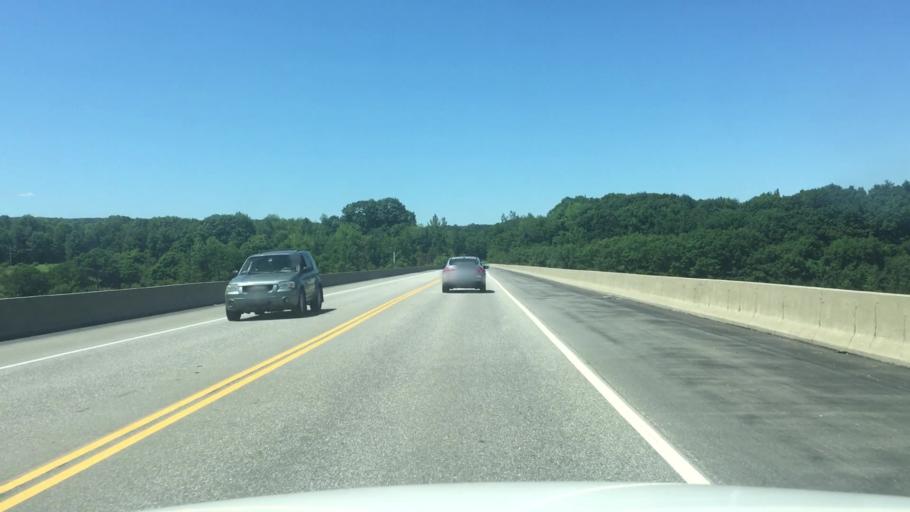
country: US
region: Maine
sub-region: Kennebec County
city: Waterville
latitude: 44.5301
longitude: -69.6455
